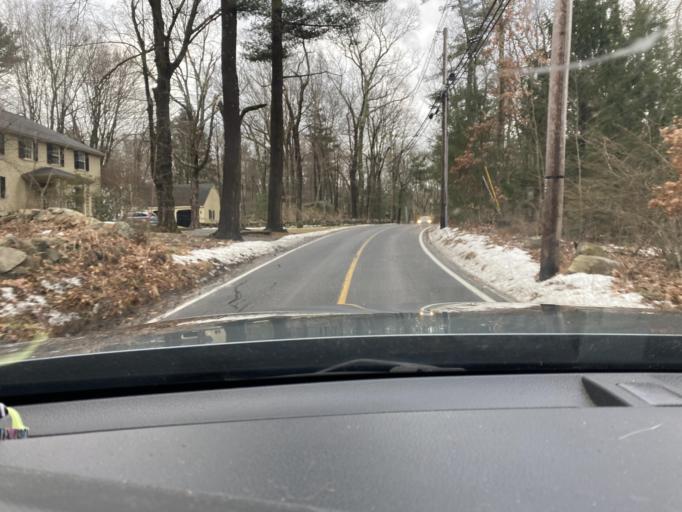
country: US
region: Massachusetts
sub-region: Middlesex County
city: Sherborn
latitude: 42.2169
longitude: -71.3783
